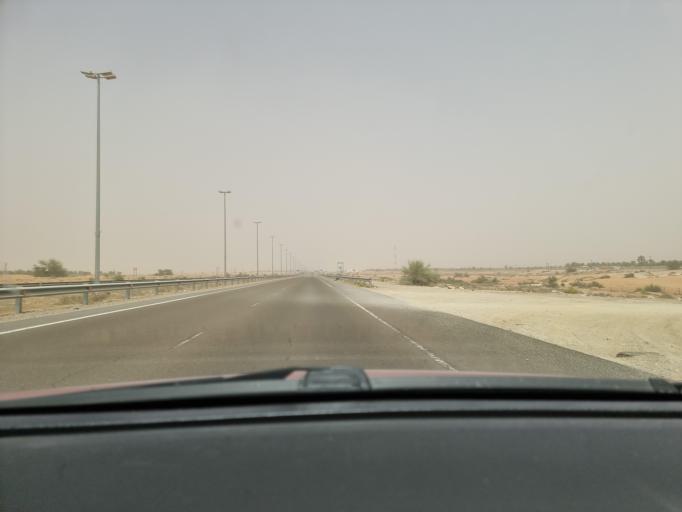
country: OM
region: Al Buraimi
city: Al Buraymi
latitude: 24.5393
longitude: 55.6207
